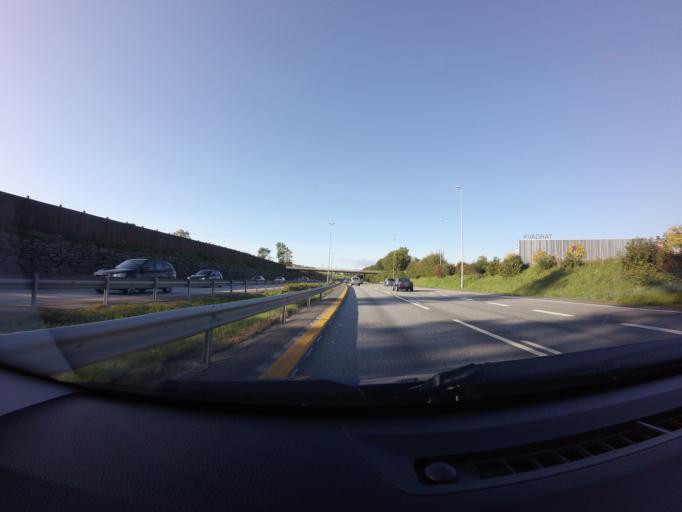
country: NO
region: Rogaland
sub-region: Sandnes
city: Sandnes
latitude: 58.8759
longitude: 5.7195
